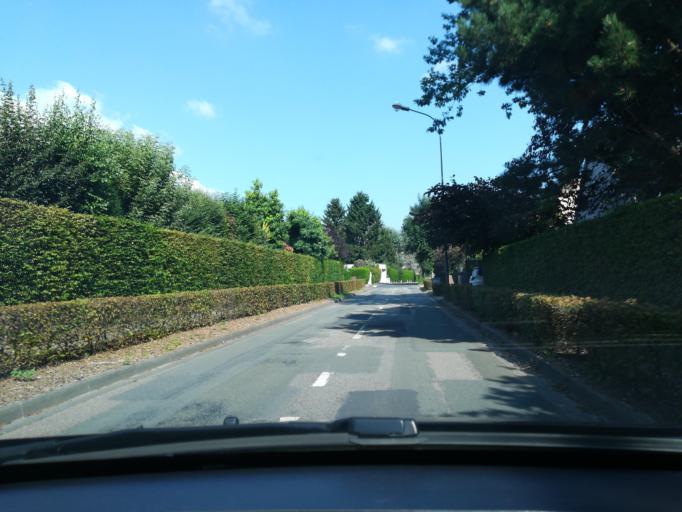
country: FR
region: Haute-Normandie
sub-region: Departement de la Seine-Maritime
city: Bois-Guillaume
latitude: 49.4654
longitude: 1.1240
